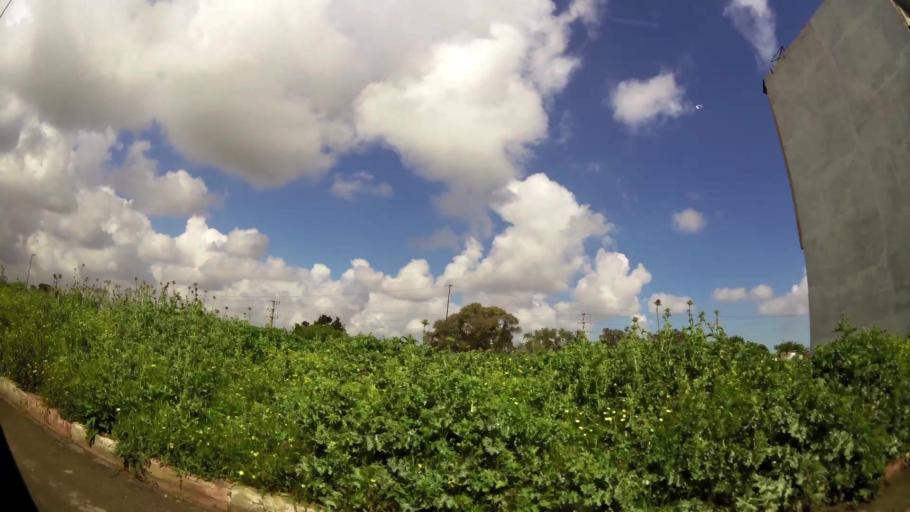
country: MA
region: Grand Casablanca
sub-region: Mediouna
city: Tit Mellil
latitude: 33.5479
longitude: -7.4909
